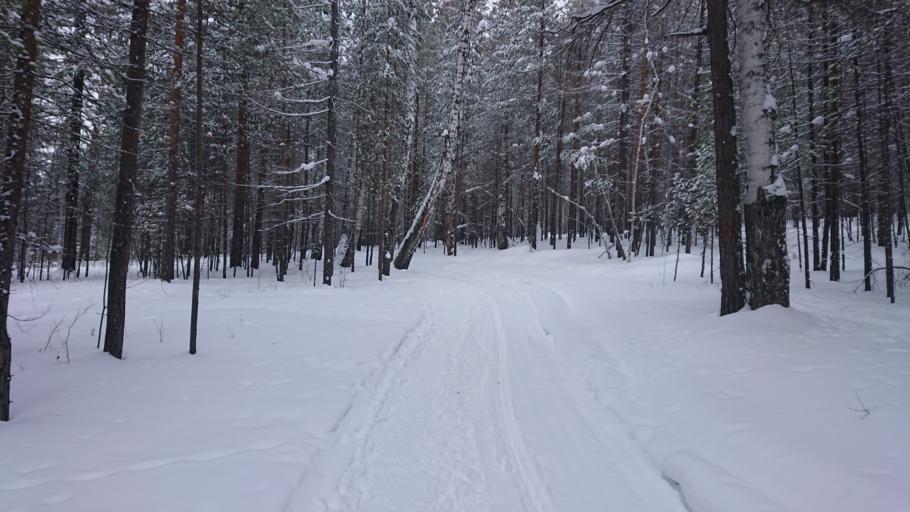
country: RU
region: Sverdlovsk
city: Degtyarsk
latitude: 56.6922
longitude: 60.0656
